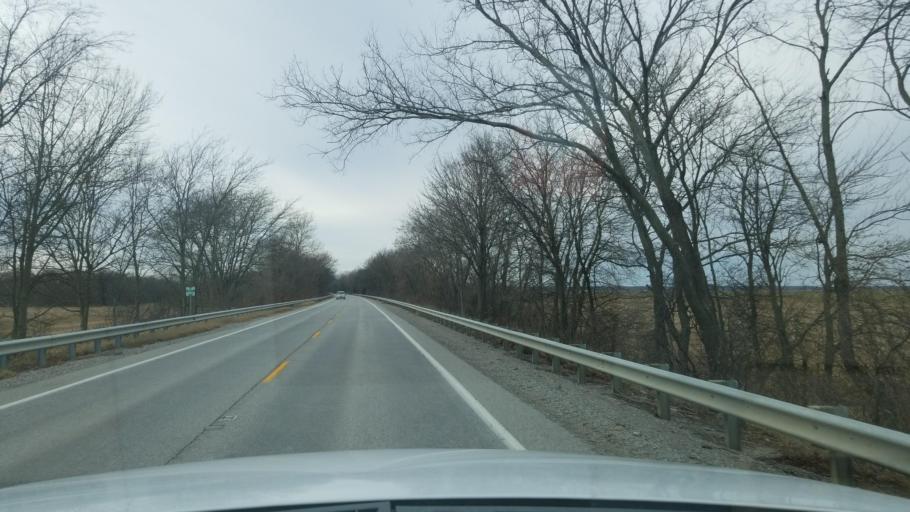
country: US
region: Indiana
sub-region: Posey County
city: Mount Vernon
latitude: 37.9425
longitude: -88.0569
